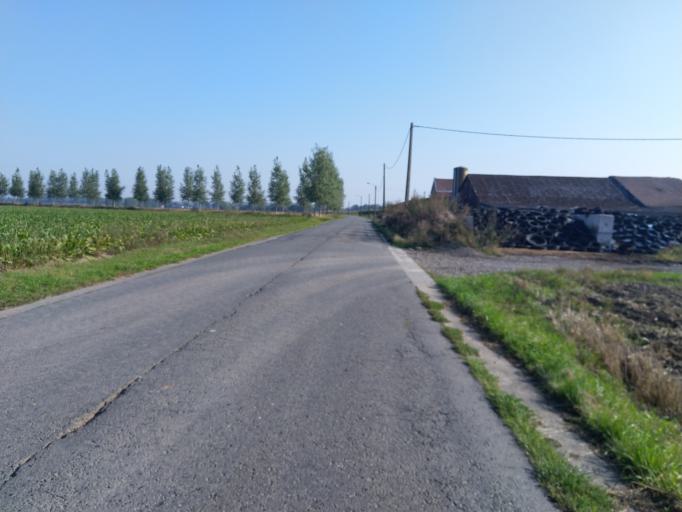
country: BE
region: Wallonia
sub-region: Province du Hainaut
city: Roeulx
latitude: 50.5356
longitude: 4.0813
